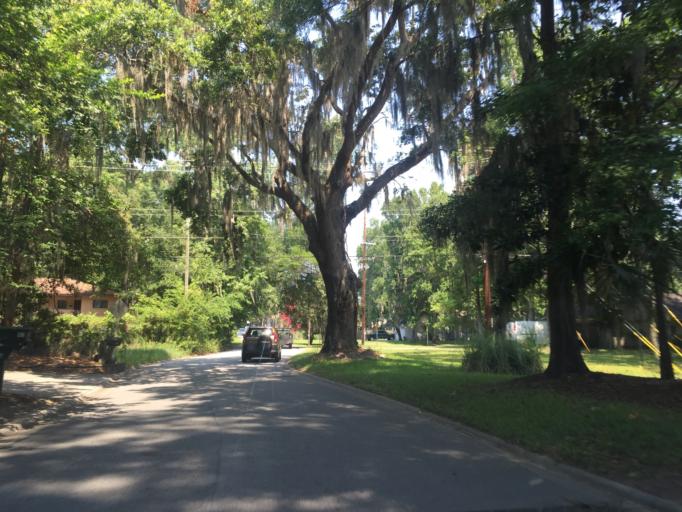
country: US
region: Georgia
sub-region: Chatham County
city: Montgomery
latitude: 31.9722
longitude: -81.1308
